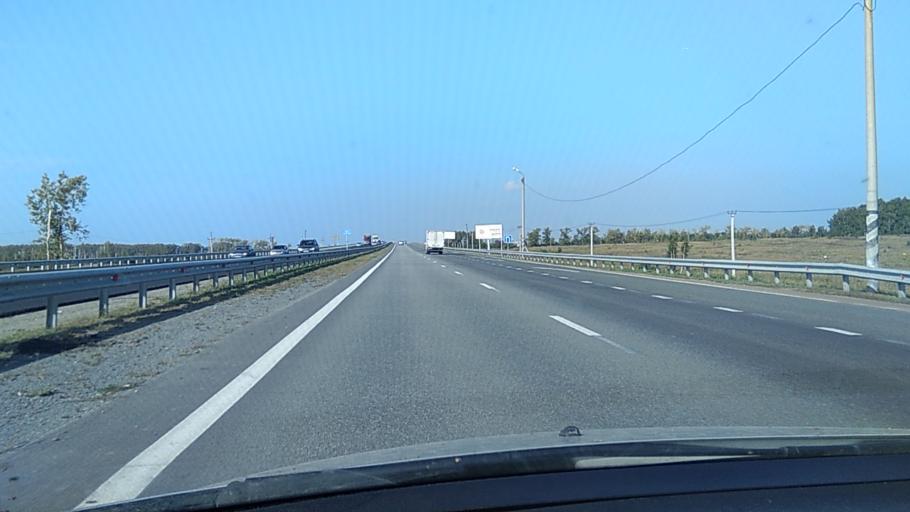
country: RU
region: Chelyabinsk
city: Sargazy
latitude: 55.0452
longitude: 61.3039
